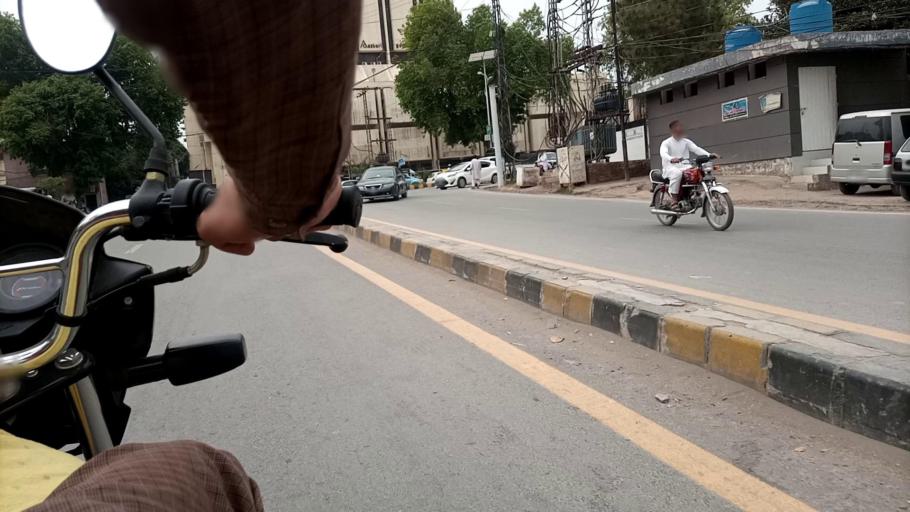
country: PK
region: Khyber Pakhtunkhwa
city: Peshawar
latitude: 33.9989
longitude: 71.5360
